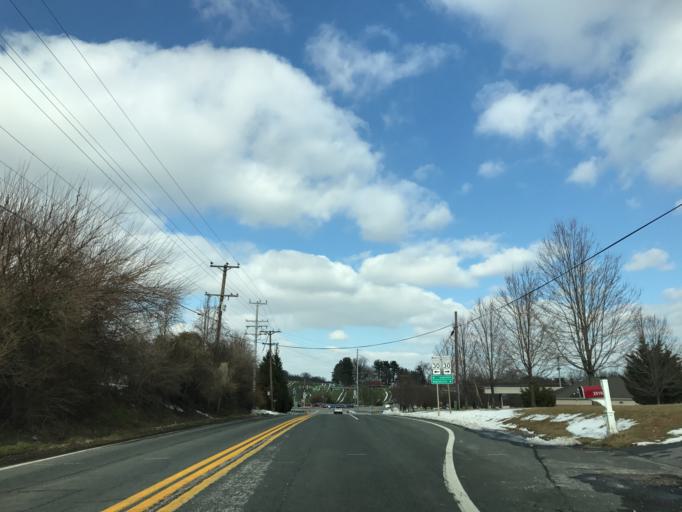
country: US
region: Maryland
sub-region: Carroll County
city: Manchester
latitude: 39.6971
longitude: -76.9062
